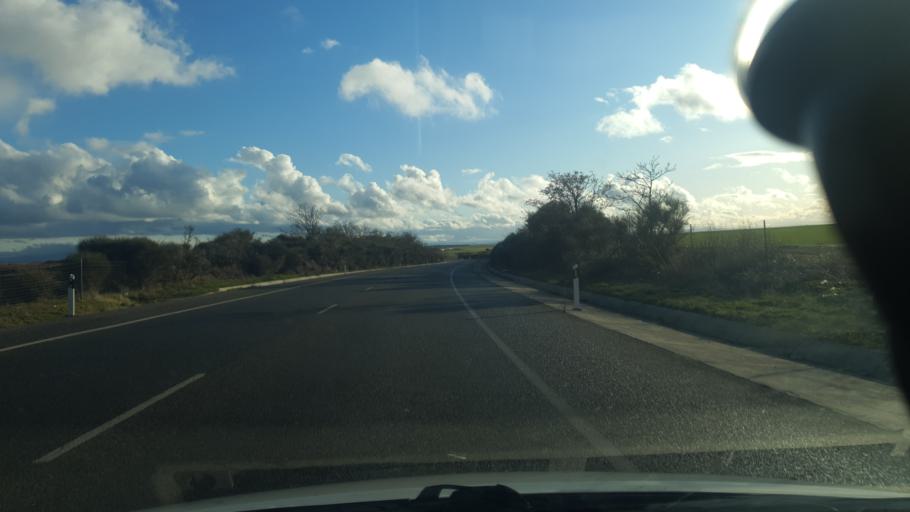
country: ES
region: Castille and Leon
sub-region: Provincia de Segovia
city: Codorniz
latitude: 41.0450
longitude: -4.6223
